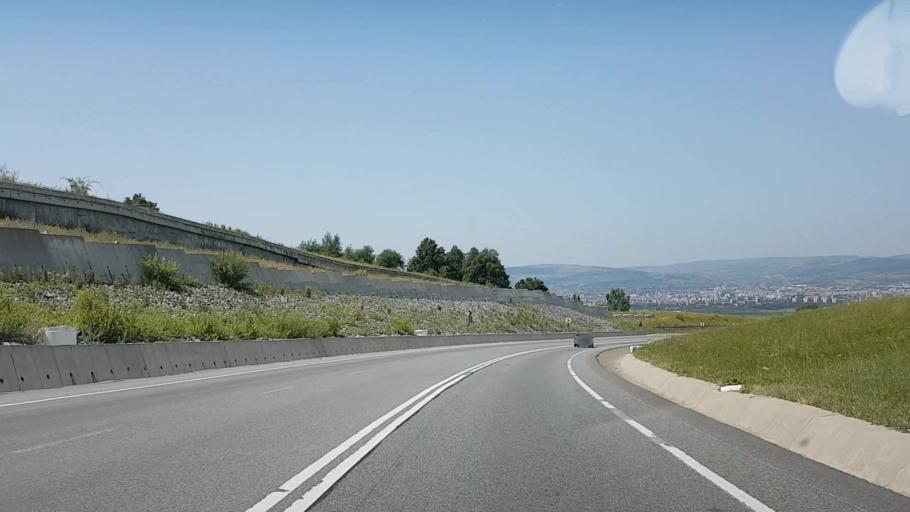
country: RO
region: Cluj
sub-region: Comuna Feleacu
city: Feleacu
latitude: 46.7226
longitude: 23.6466
